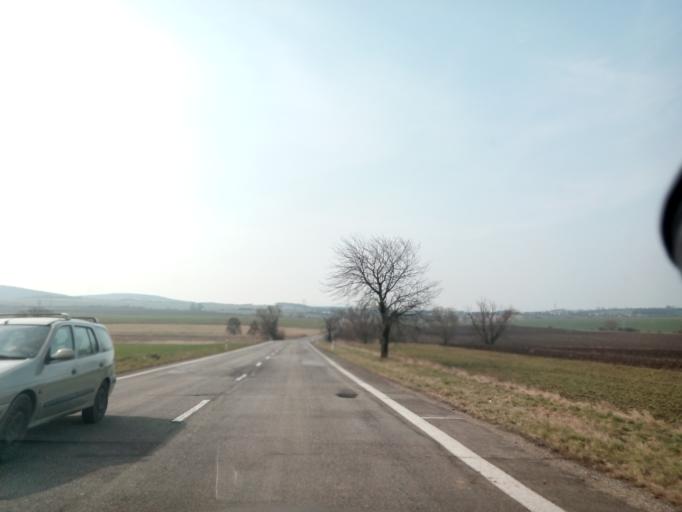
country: SK
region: Kosicky
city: Trebisov
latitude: 48.5388
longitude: 21.6826
